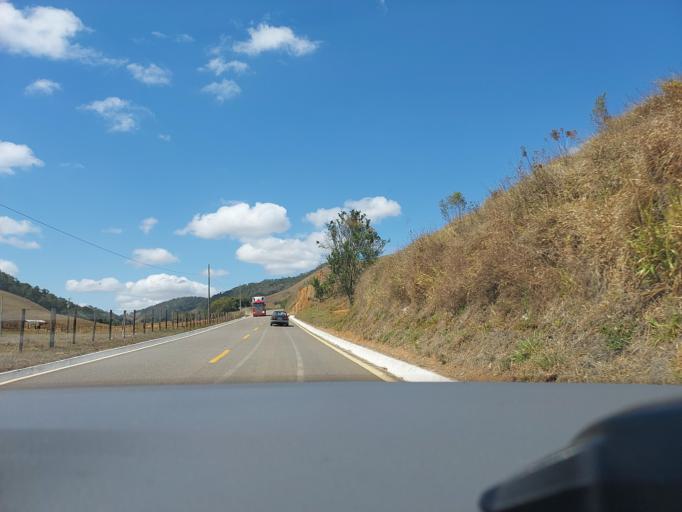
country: BR
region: Minas Gerais
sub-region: Muriae
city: Muriae
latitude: -21.0557
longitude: -42.5052
